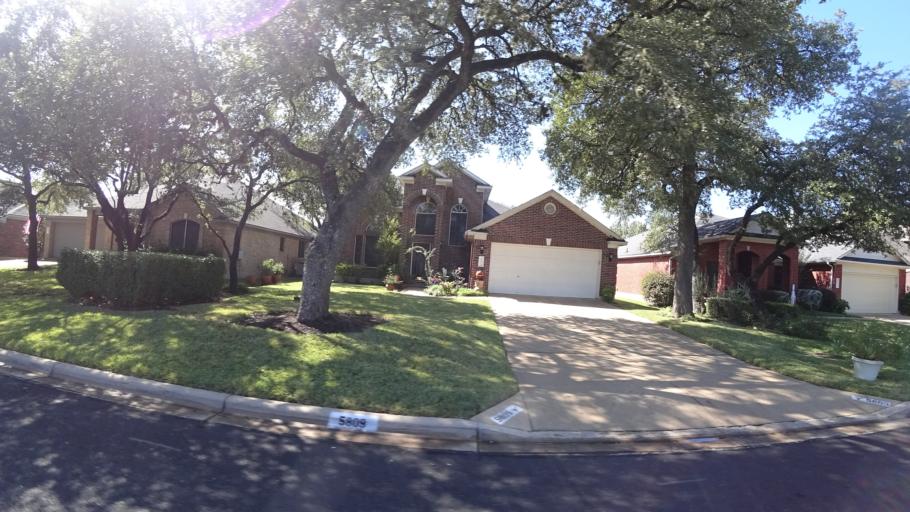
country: US
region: Texas
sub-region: Travis County
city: Shady Hollow
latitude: 30.2099
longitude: -97.8714
